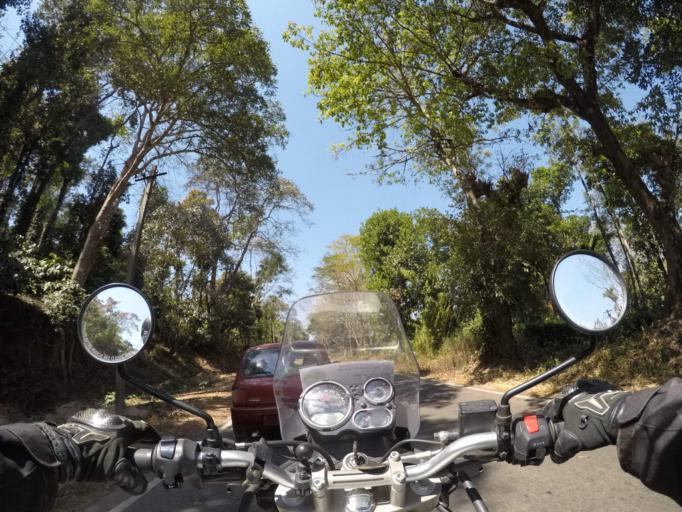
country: IN
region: Karnataka
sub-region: Hassan
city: Sakleshpur
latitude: 12.9550
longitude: 75.7483
